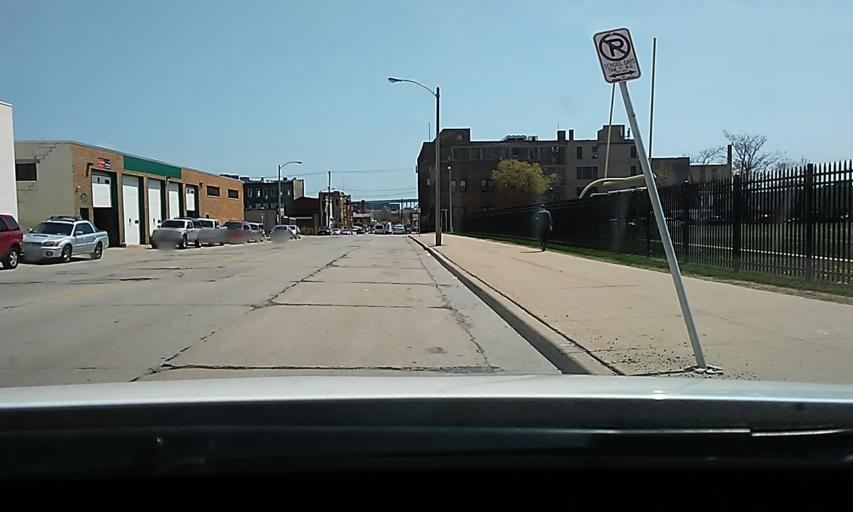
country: US
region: Wisconsin
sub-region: Milwaukee County
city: Milwaukee
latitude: 43.0263
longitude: -87.9152
